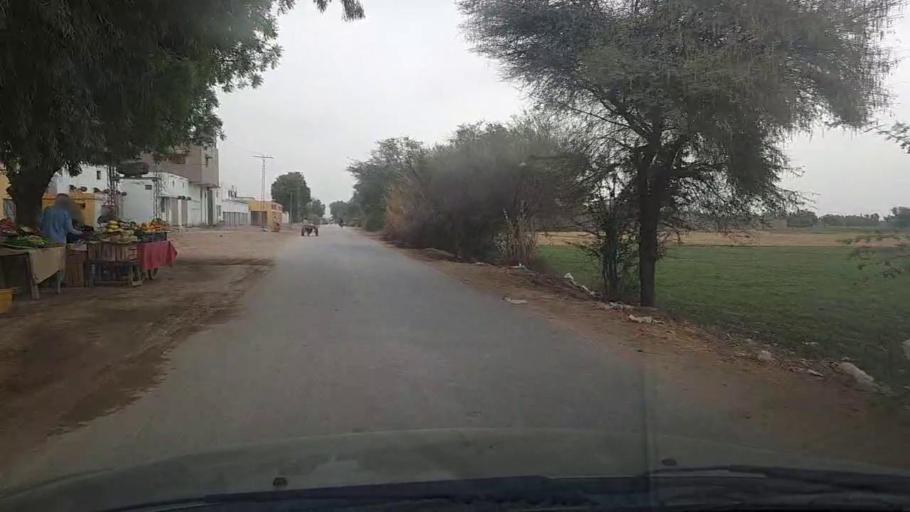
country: PK
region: Sindh
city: Daulatpur
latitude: 26.3112
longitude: 68.1014
